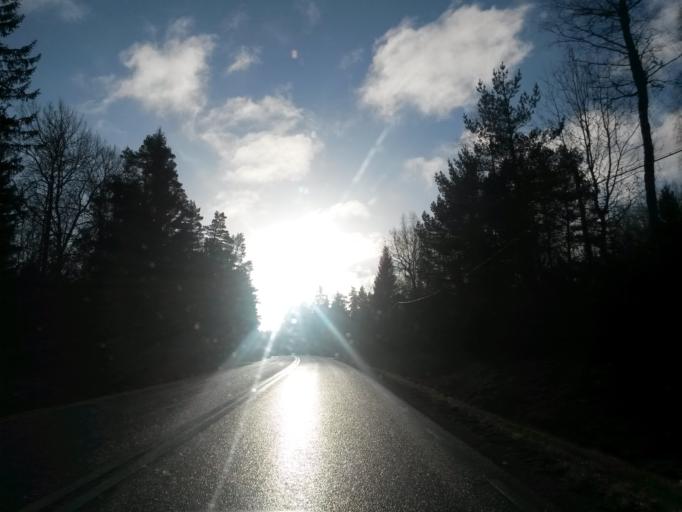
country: SE
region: Vaestra Goetaland
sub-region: Vargarda Kommun
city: Vargarda
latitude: 57.9718
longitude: 12.8116
